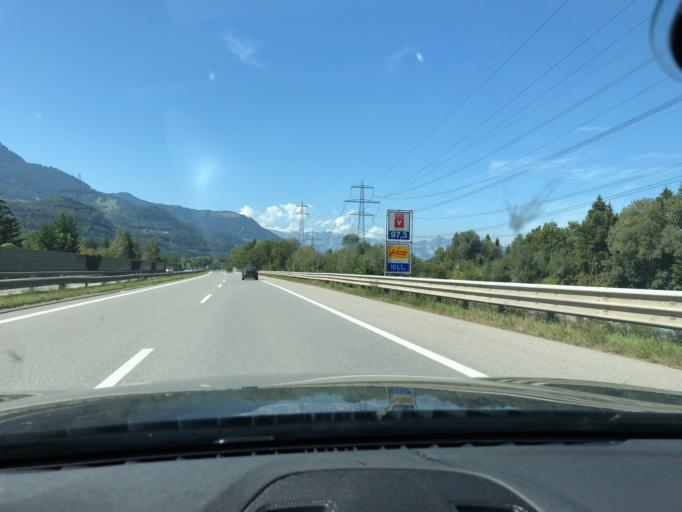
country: AT
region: Vorarlberg
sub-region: Politischer Bezirk Feldkirch
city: Schlins
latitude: 47.1958
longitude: 9.7063
